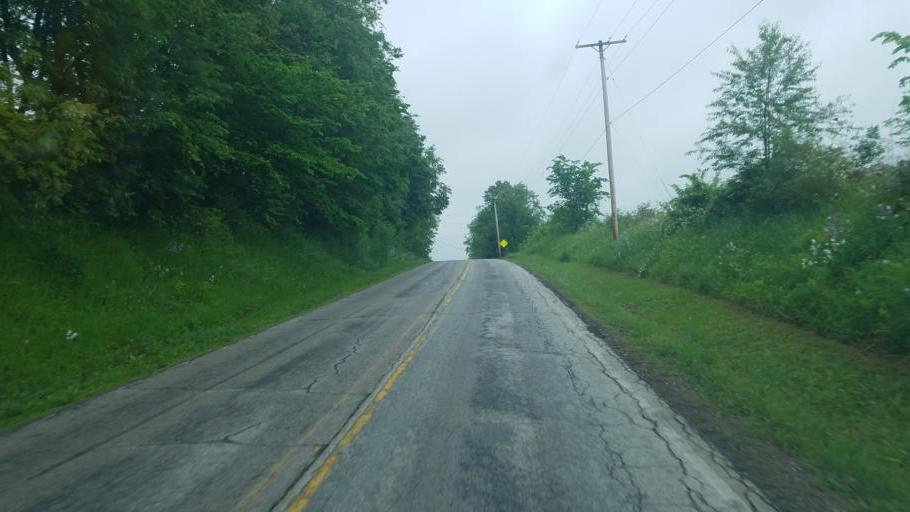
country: US
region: Ohio
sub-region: Richland County
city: Mansfield
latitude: 40.6922
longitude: -82.4728
